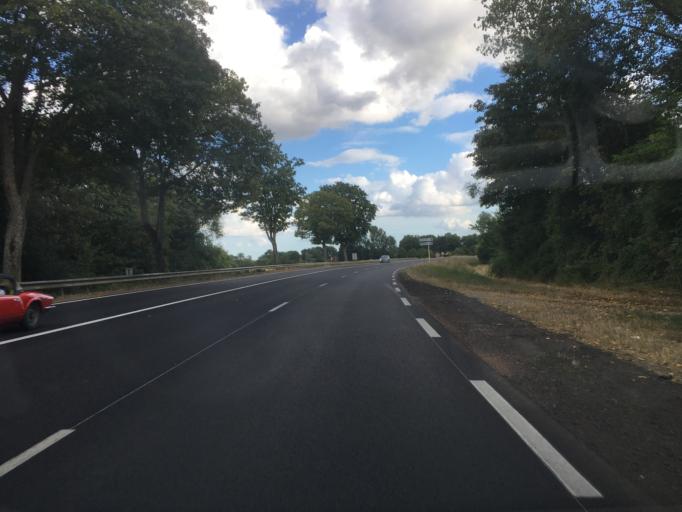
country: FR
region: Bourgogne
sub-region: Departement de l'Yonne
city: Cheny
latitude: 47.9341
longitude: 3.5101
